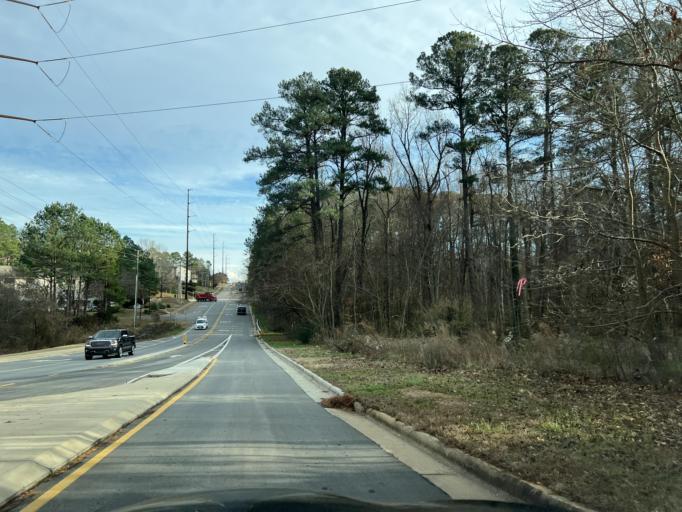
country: US
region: North Carolina
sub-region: Wake County
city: Cary
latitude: 35.8045
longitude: -78.7362
